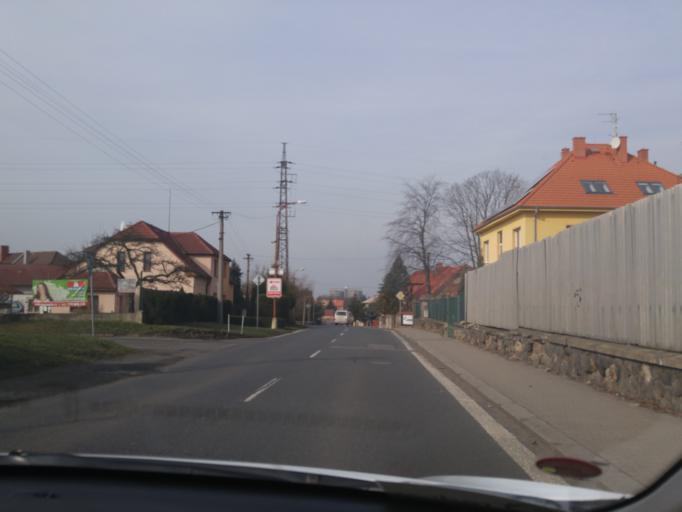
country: CZ
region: Central Bohemia
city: Kostelec nad Labem
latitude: 50.2234
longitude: 14.5898
